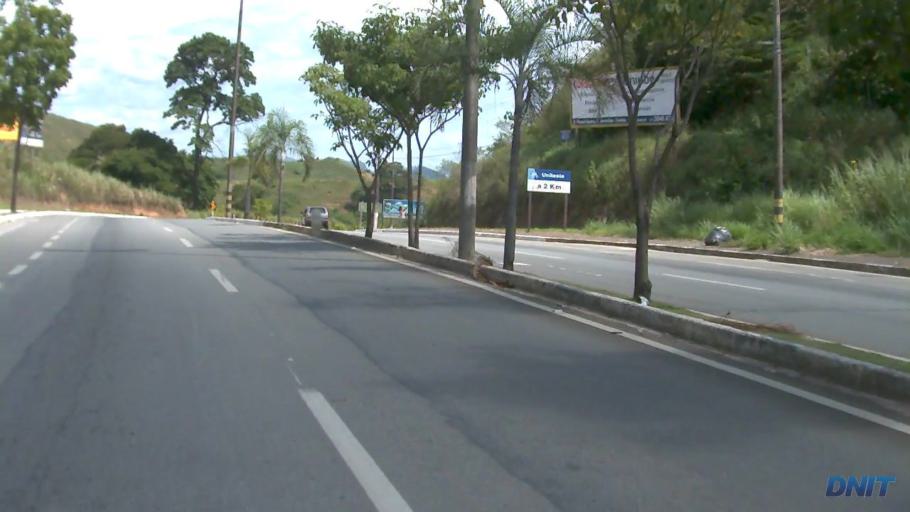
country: BR
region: Minas Gerais
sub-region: Coronel Fabriciano
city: Coronel Fabriciano
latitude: -19.5050
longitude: -42.5922
